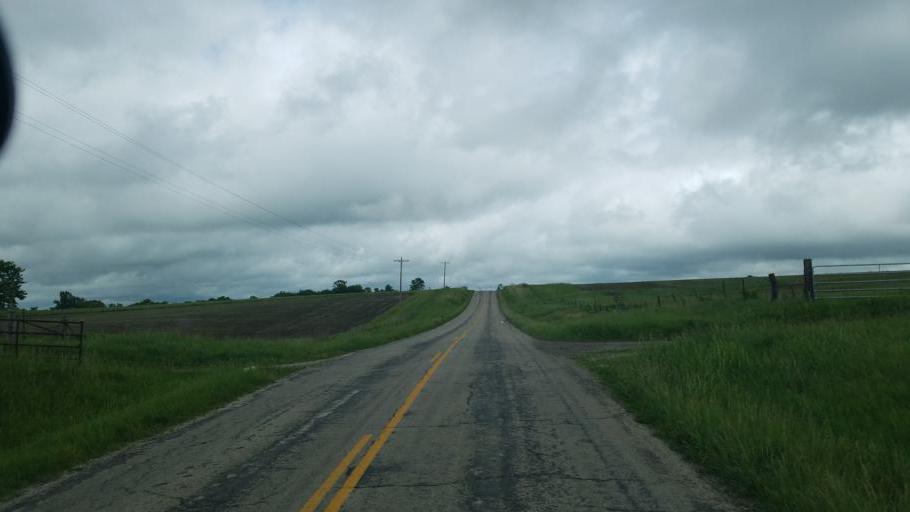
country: US
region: Missouri
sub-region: Mercer County
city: Princeton
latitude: 40.3553
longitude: -93.6807
